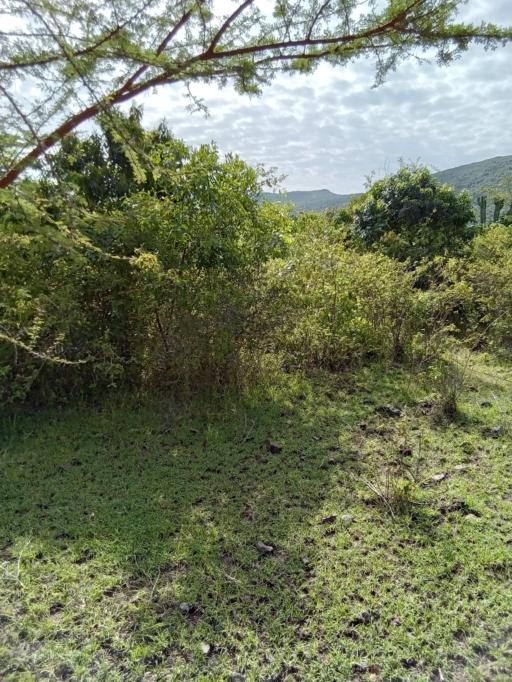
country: KE
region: Homa Bay
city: Homa Bay
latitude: -0.4805
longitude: 34.1749
